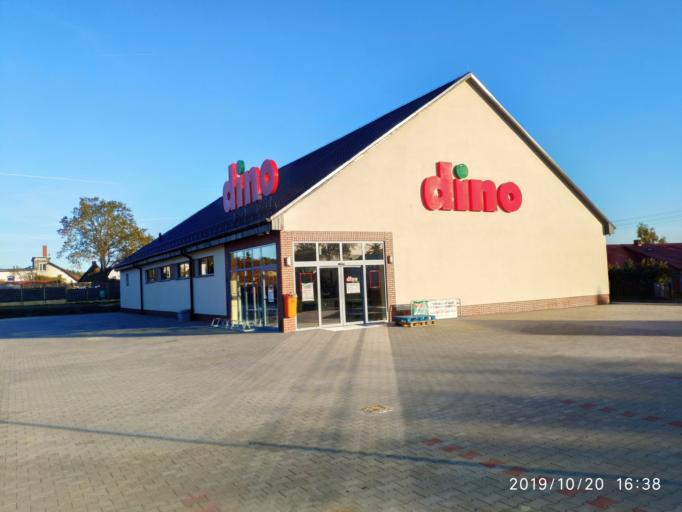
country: PL
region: Lubusz
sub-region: Powiat zielonogorski
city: Ochla
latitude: 51.8821
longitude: 15.4734
